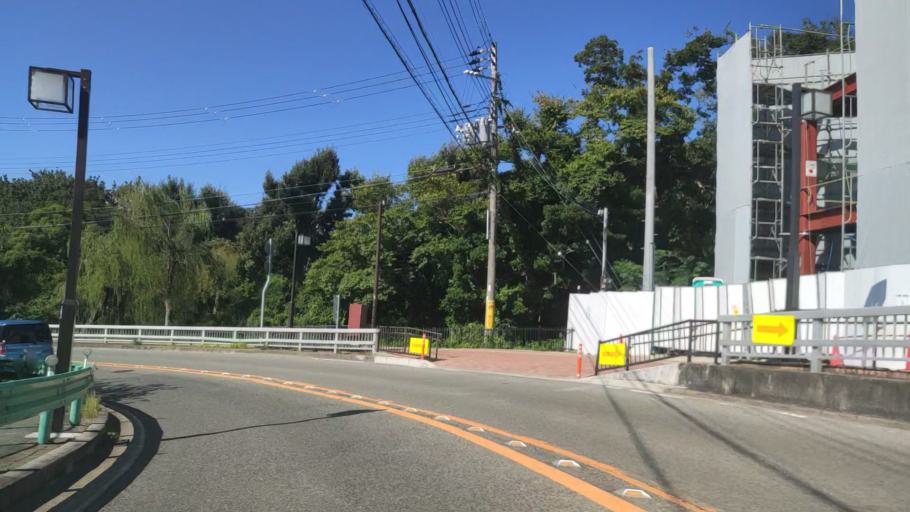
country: JP
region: Hyogo
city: Akashi
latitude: 34.6513
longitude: 134.9948
